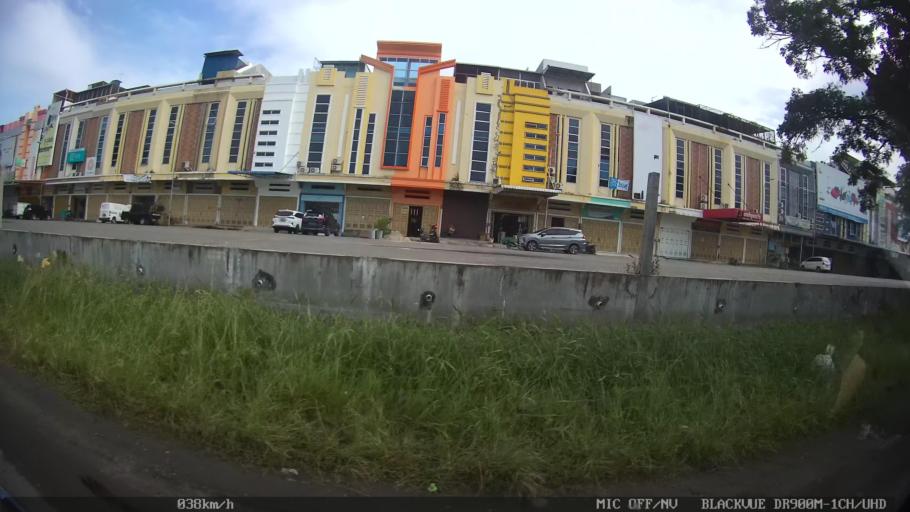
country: ID
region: North Sumatra
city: Medan
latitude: 3.6287
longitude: 98.7042
